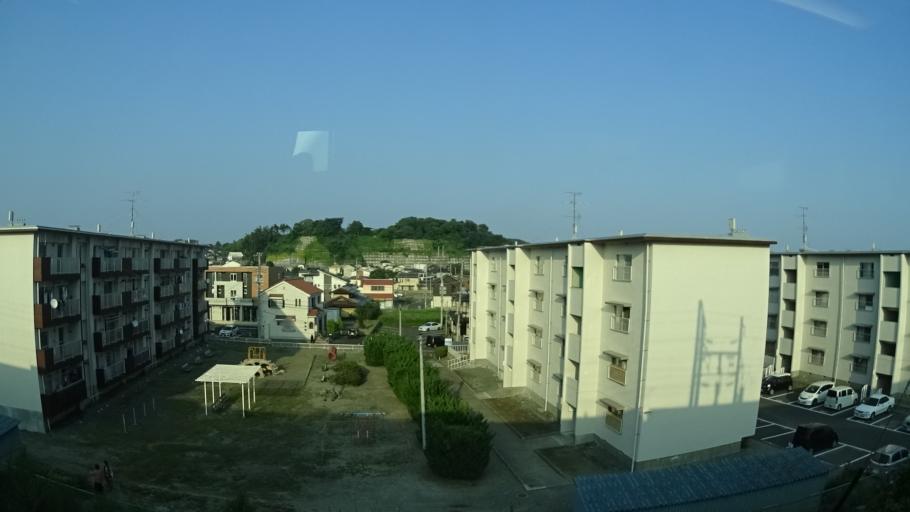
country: JP
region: Ibaraki
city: Funaishikawa
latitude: 36.4991
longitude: 140.6104
